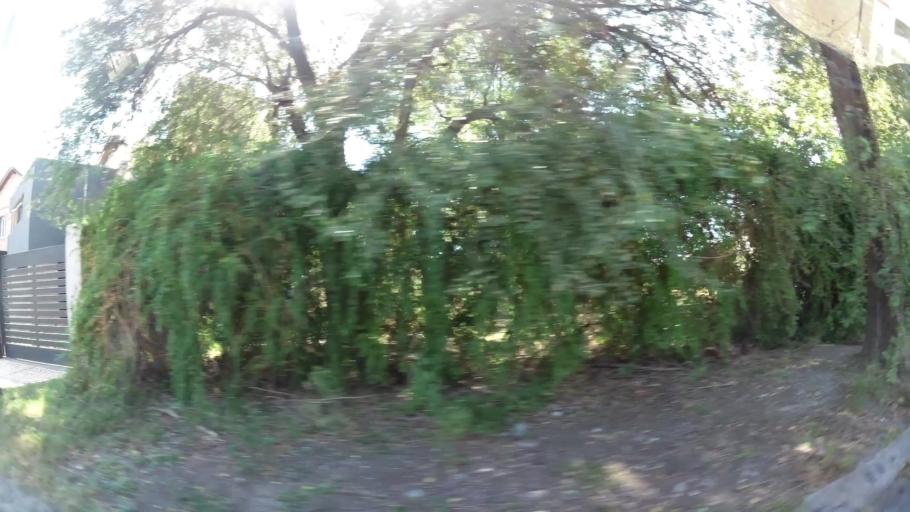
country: AR
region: Cordoba
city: Villa Allende
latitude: -31.2930
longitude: -64.2818
